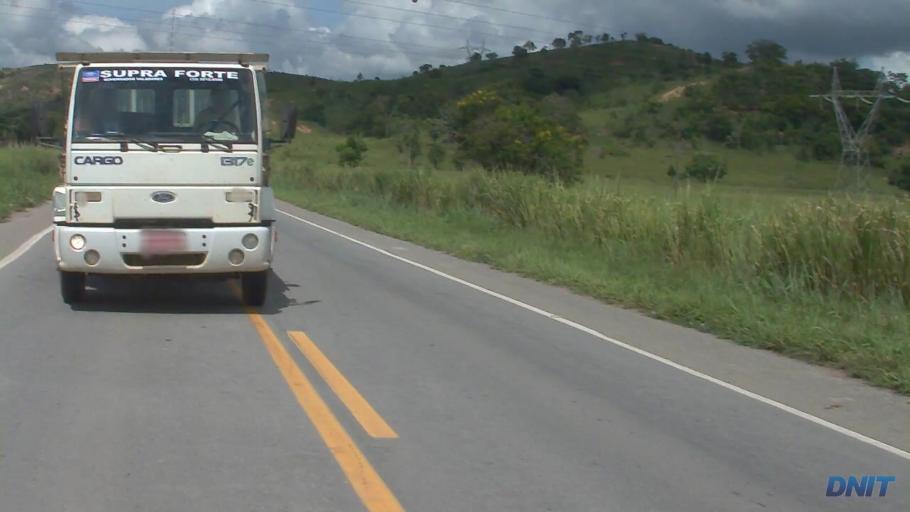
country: BR
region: Minas Gerais
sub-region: Governador Valadares
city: Governador Valadares
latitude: -19.0188
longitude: -42.1421
